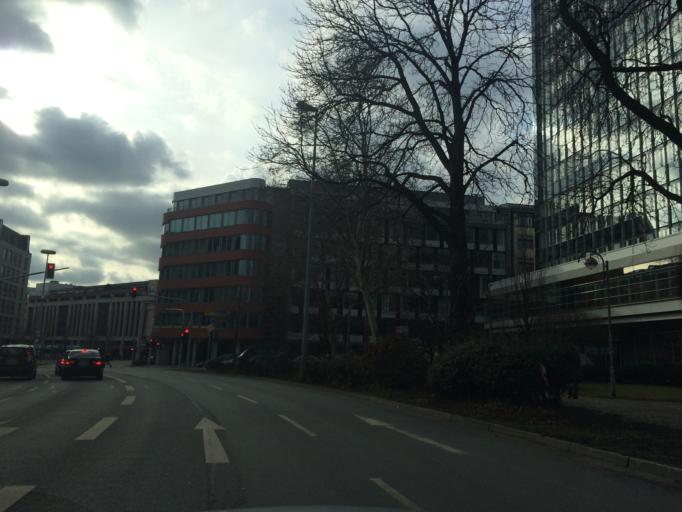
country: DE
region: Hesse
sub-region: Regierungsbezirk Darmstadt
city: Frankfurt am Main
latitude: 50.1184
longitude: 8.6885
